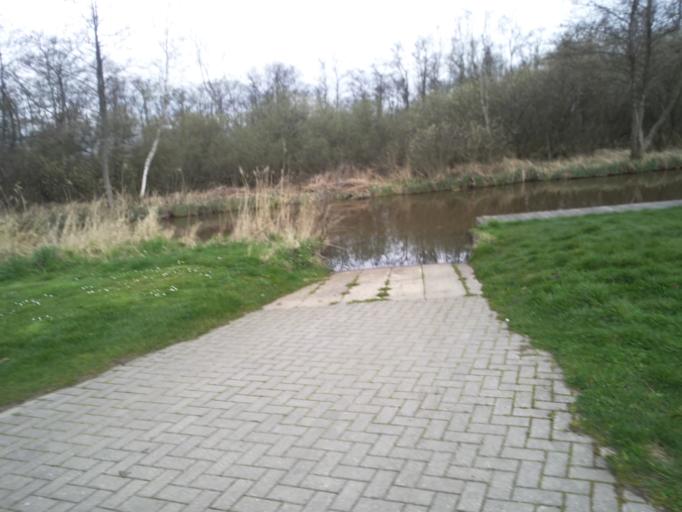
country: NL
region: Overijssel
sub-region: Gemeente Steenwijkerland
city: Oldemarkt
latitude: 52.7816
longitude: 5.9831
